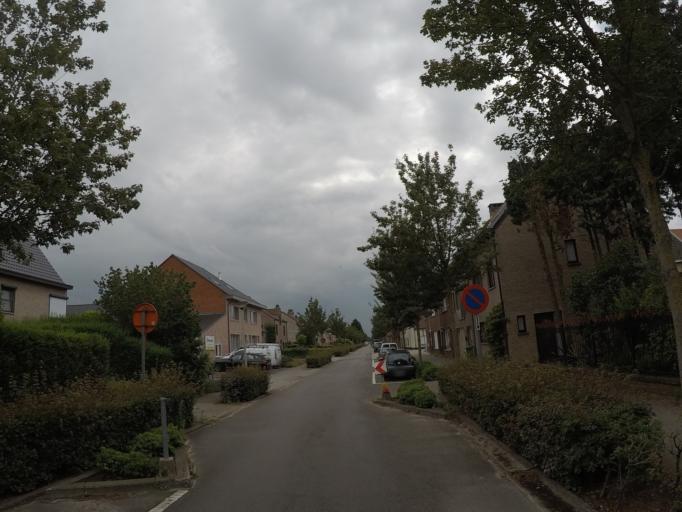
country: BE
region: Flanders
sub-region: Provincie Antwerpen
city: Kapellen
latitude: 51.3029
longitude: 4.4130
